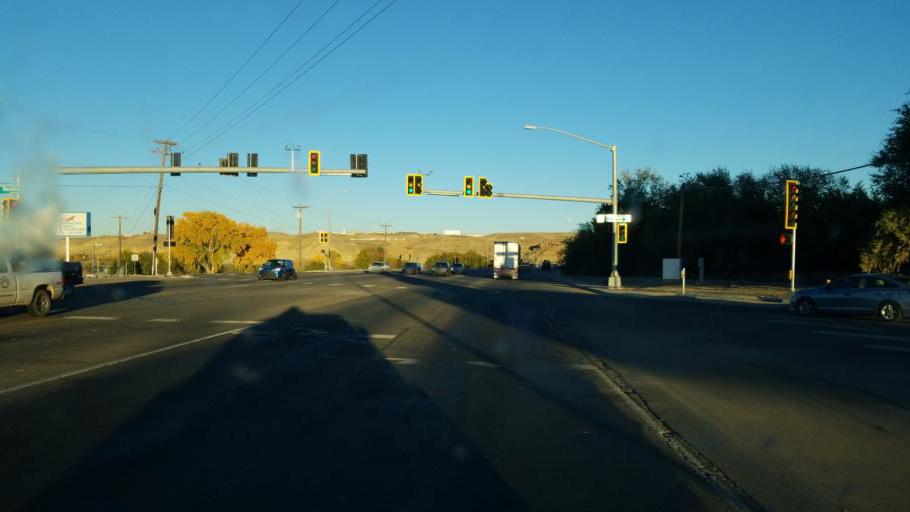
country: US
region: New Mexico
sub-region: San Juan County
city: Farmington
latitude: 36.7334
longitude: -108.2445
